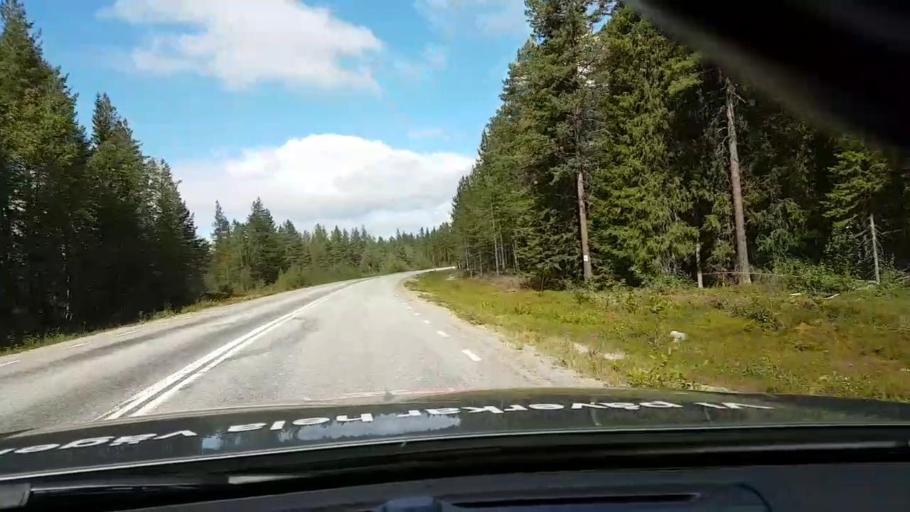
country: SE
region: Vaesternorrland
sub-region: OErnskoeldsviks Kommun
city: Bredbyn
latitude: 63.6070
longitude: 17.9000
